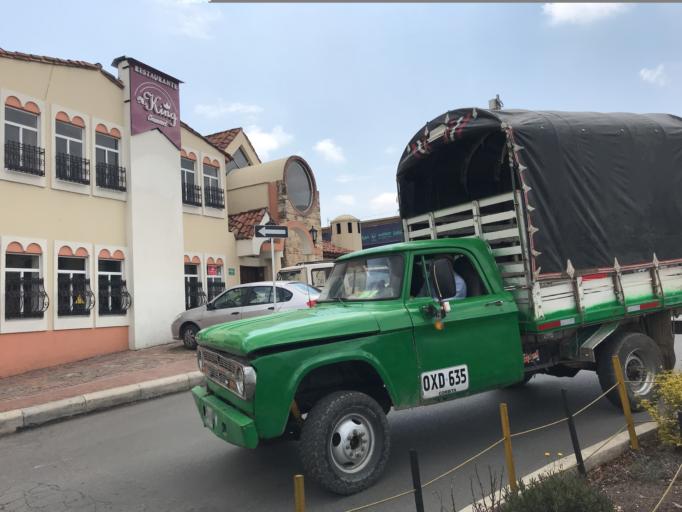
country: CO
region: Boyaca
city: Tunja
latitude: 5.5377
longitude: -73.3602
